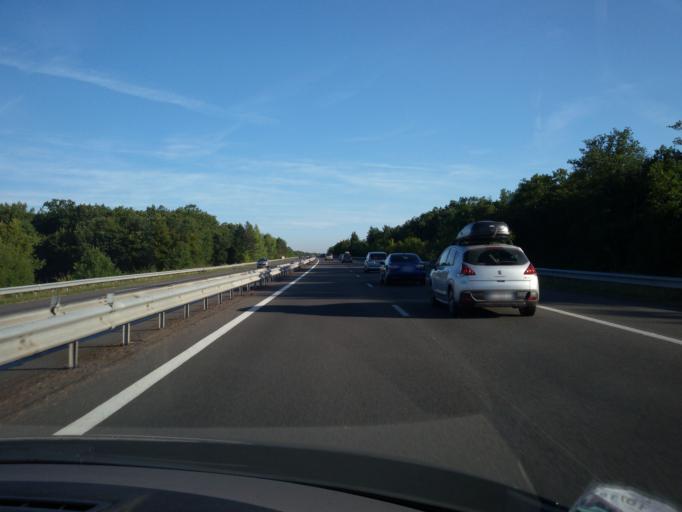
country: FR
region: Centre
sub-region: Departement du Cher
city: Levet
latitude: 46.8713
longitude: 2.4255
